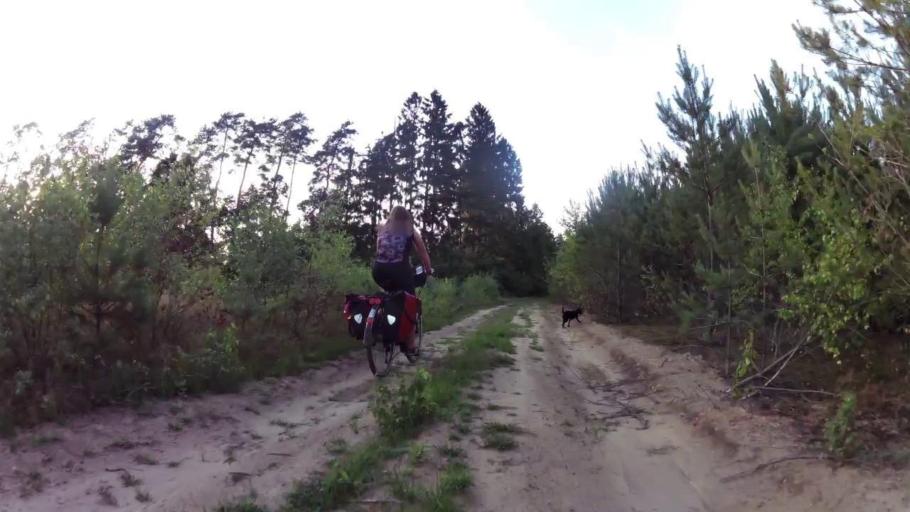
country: PL
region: West Pomeranian Voivodeship
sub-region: Powiat drawski
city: Drawsko Pomorskie
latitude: 53.4950
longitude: 15.7646
